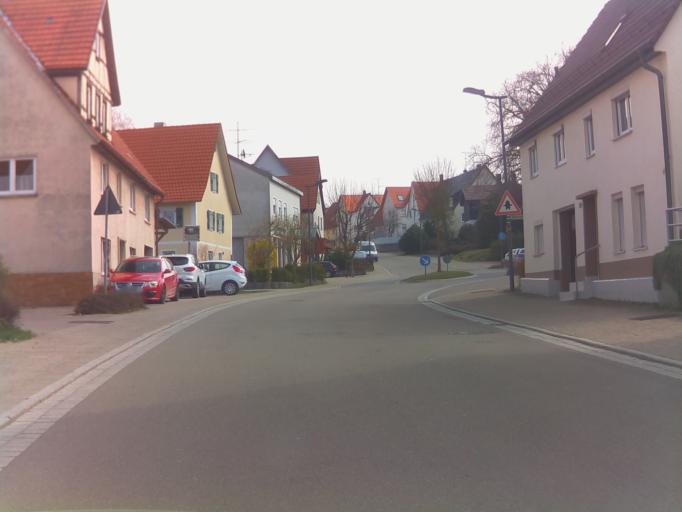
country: DE
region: Baden-Wuerttemberg
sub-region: Tuebingen Region
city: Munsingen
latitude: 48.4126
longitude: 9.5194
